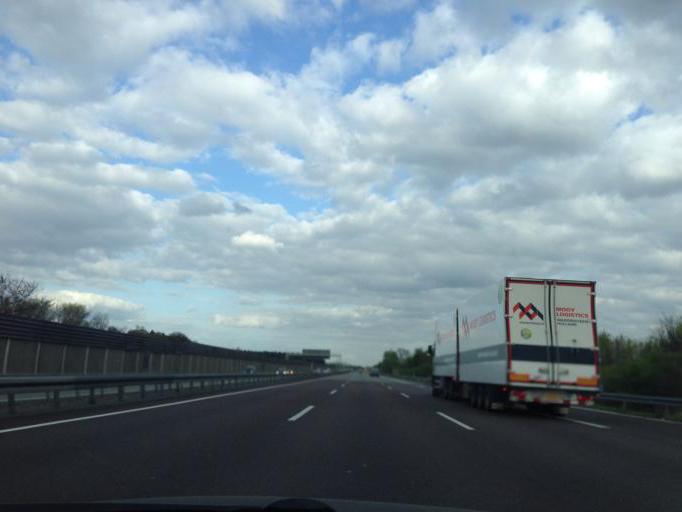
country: DE
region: Lower Saxony
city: Lehre
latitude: 52.3097
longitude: 10.6336
